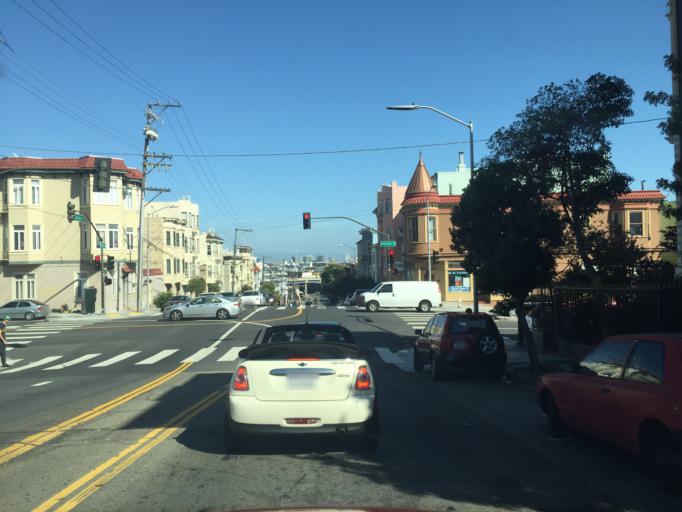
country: US
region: California
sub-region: San Francisco County
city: San Francisco
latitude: 37.7697
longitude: -122.4250
